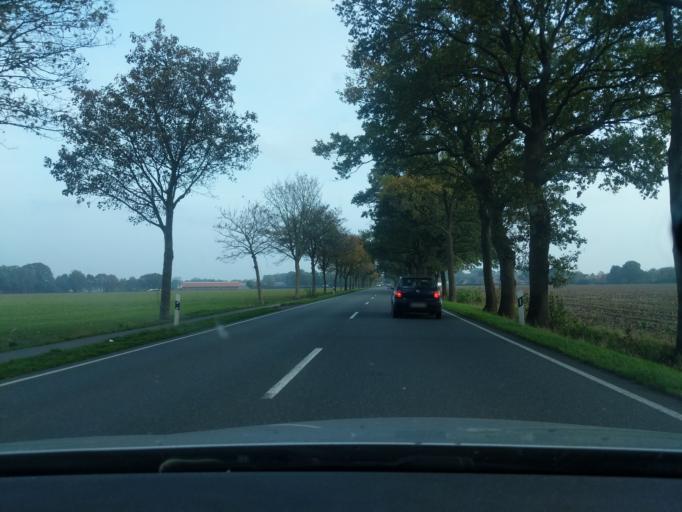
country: DE
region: Lower Saxony
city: Dudenbuttel
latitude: 53.5940
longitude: 9.3353
